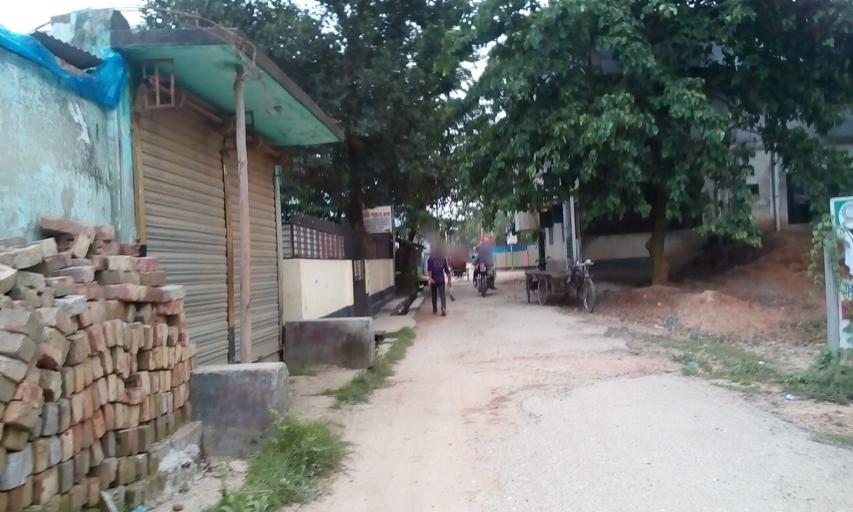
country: IN
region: West Bengal
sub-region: Dakshin Dinajpur
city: Balurghat
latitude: 25.3831
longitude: 88.9926
